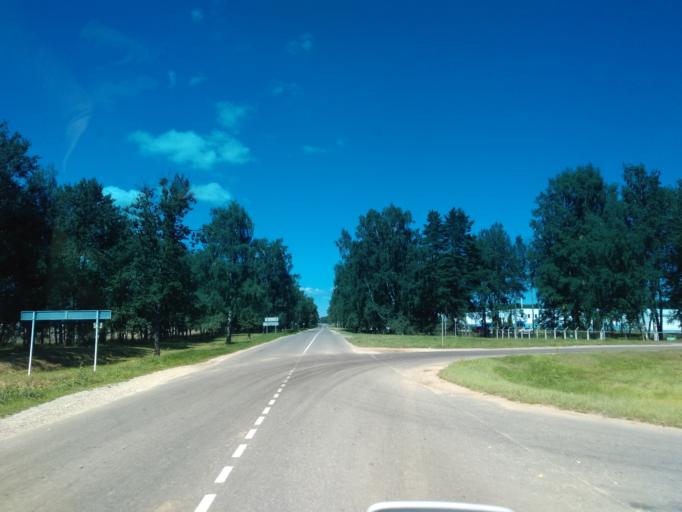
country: BY
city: Fanipol
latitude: 53.7241
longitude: 27.3373
